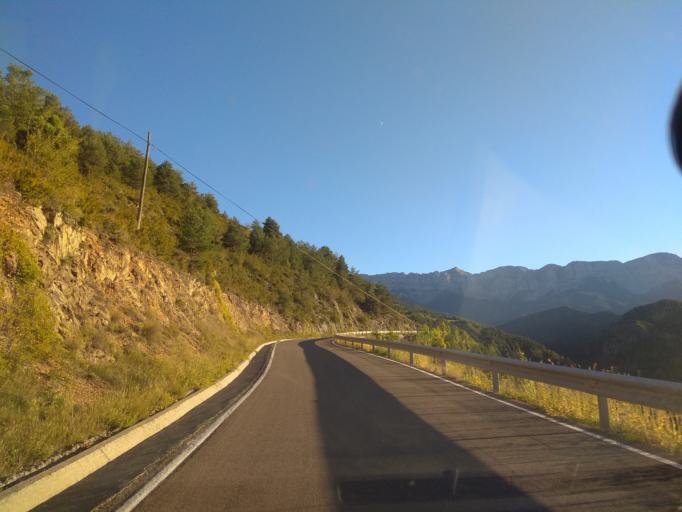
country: ES
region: Catalonia
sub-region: Provincia de Lleida
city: Lles de Cerdanya
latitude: 42.3526
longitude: 1.6896
